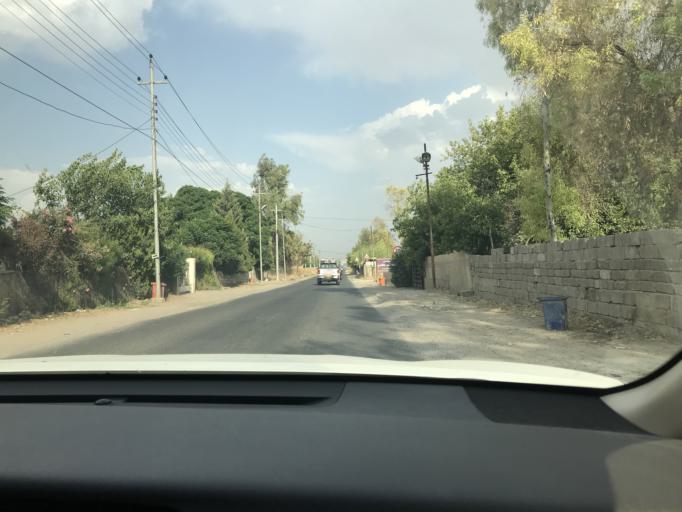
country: IQ
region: Arbil
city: Erbil
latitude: 36.2076
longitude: 43.9578
